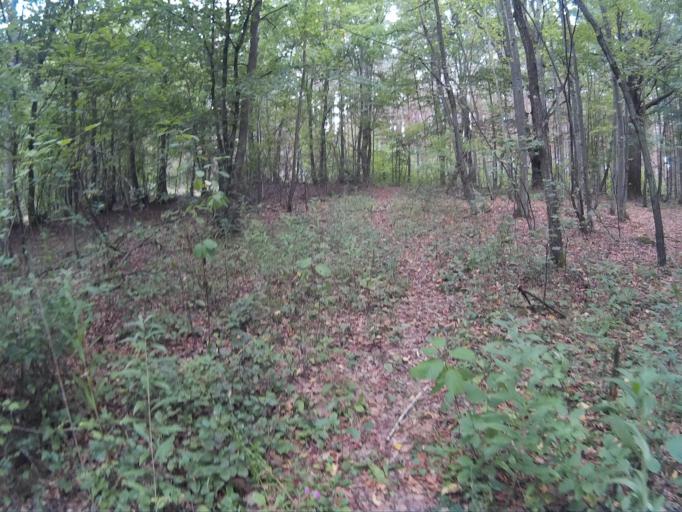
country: HU
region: Zala
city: Zalalovo
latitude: 46.7931
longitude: 16.5285
